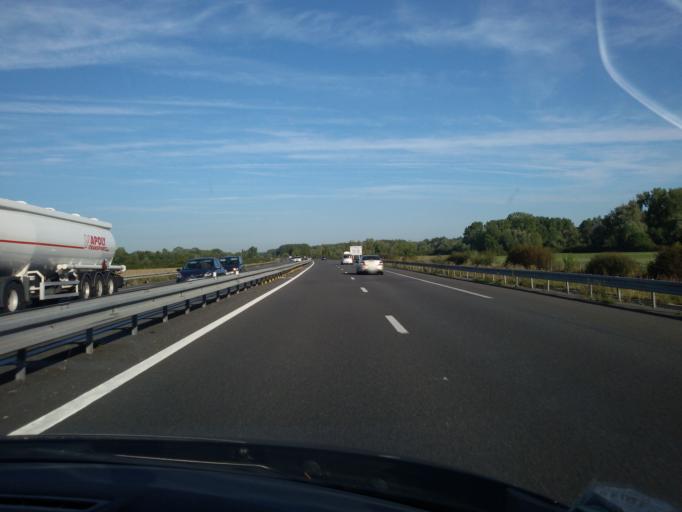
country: FR
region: Centre
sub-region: Departement du Cher
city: Vignoux-sur-Barangeon
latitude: 47.1937
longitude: 2.1565
